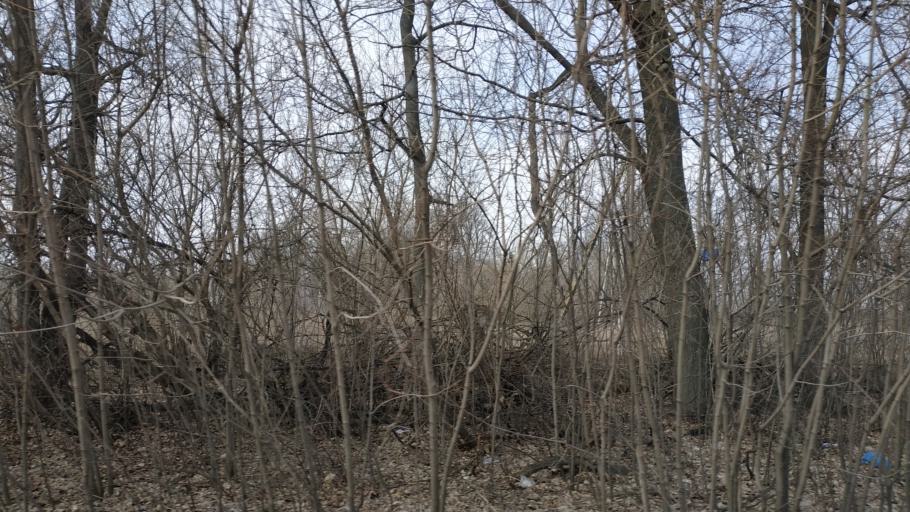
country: RU
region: Moskovskaya
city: Malyshevo
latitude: 55.4001
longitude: 38.3601
